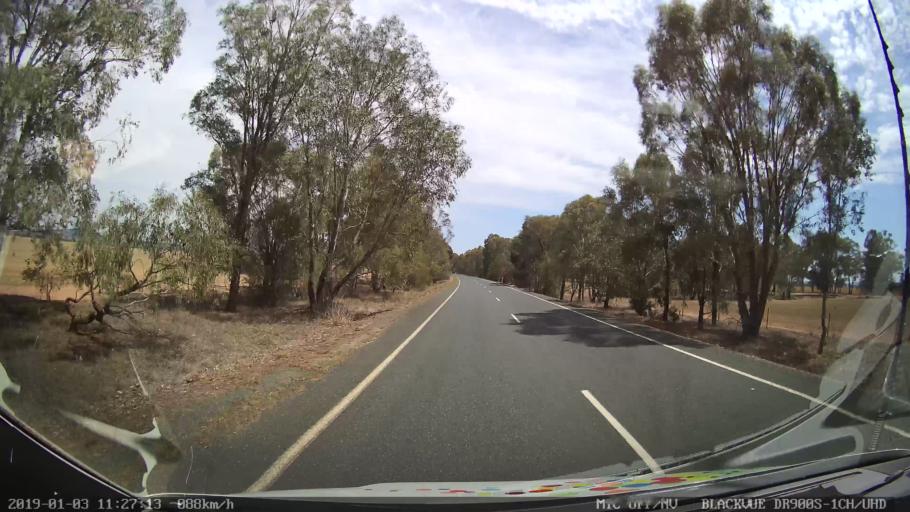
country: AU
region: New South Wales
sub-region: Weddin
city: Grenfell
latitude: -34.0152
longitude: 148.2205
